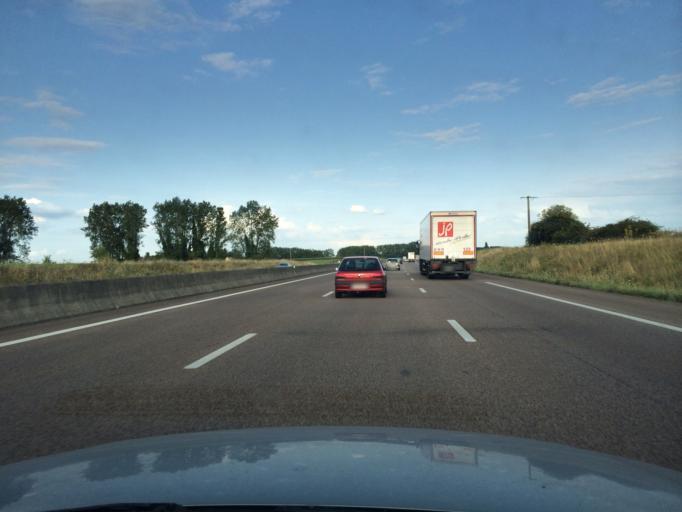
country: FR
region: Haute-Normandie
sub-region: Departement de l'Eure
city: Hauville
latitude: 49.3697
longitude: 0.7662
